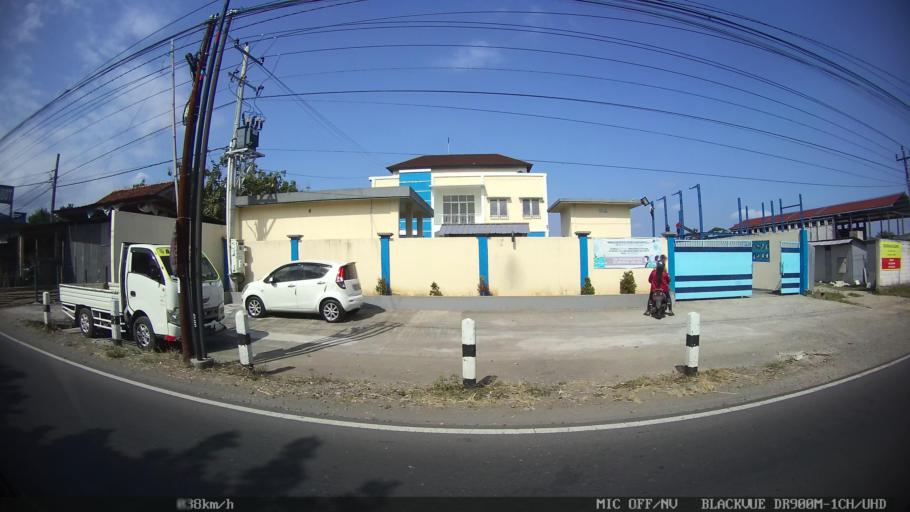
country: ID
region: Daerah Istimewa Yogyakarta
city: Sewon
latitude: -7.8568
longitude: 110.3900
